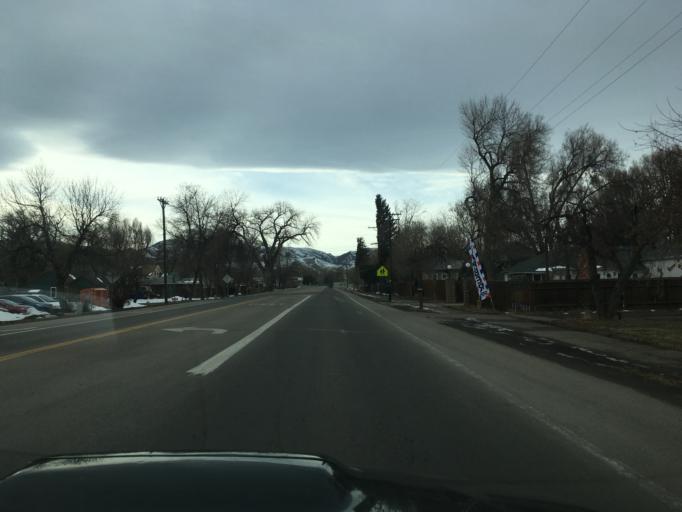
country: US
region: Colorado
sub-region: Larimer County
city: Laporte
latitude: 40.6272
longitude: -105.1388
